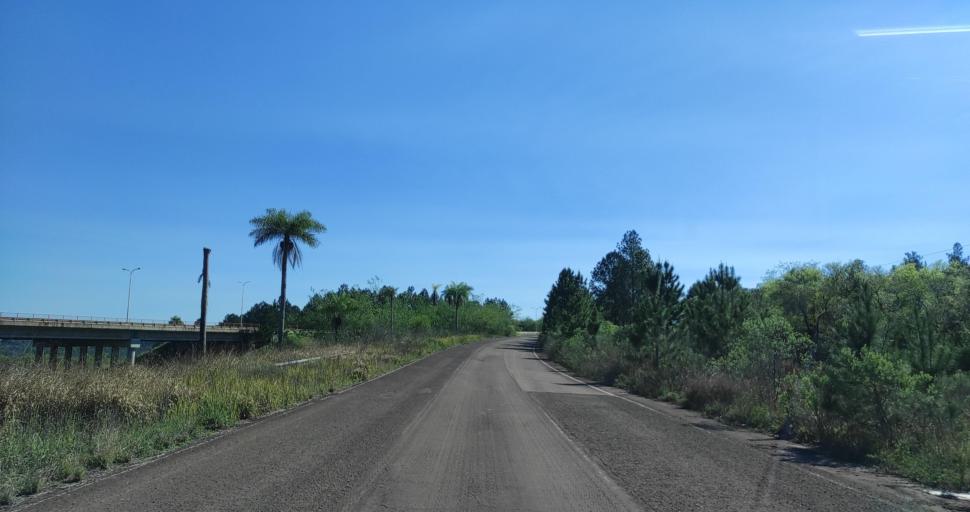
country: AR
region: Misiones
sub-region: Departamento de Candelaria
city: Loreto
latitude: -27.3052
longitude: -55.5385
